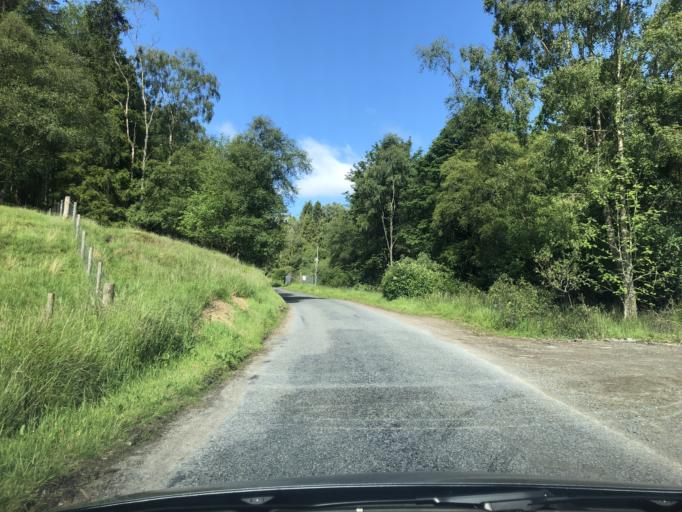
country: GB
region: Scotland
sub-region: Angus
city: Kirriemuir
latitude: 56.7338
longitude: -3.0161
